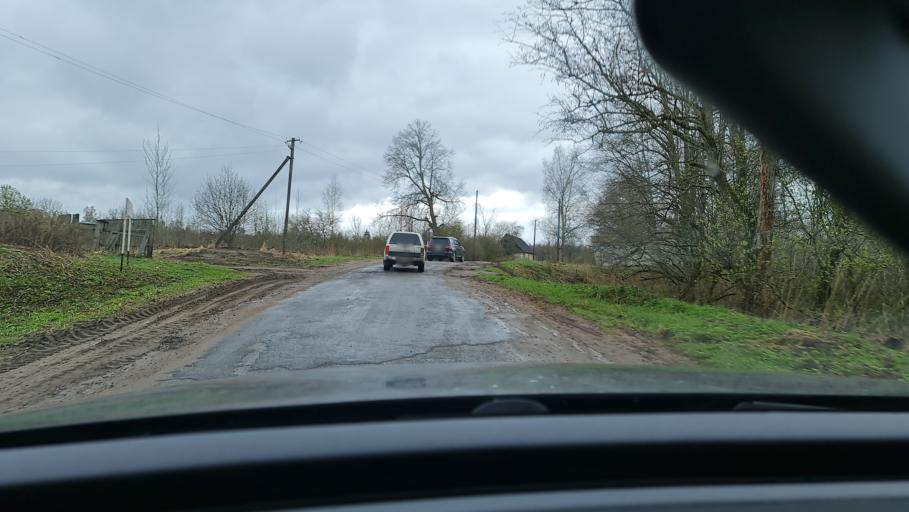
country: RU
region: Novgorod
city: Marevo
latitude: 57.2401
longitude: 32.0417
